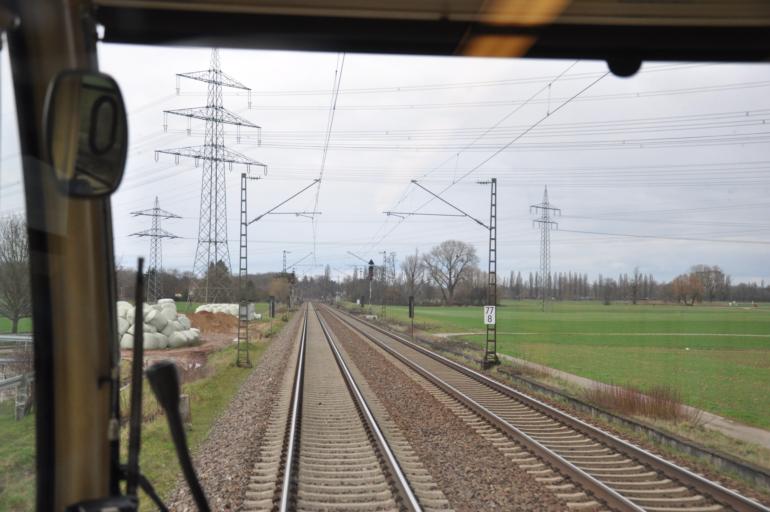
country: DE
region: Baden-Wuerttemberg
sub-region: Karlsruhe Region
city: Ettlingen
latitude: 48.9634
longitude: 8.3909
